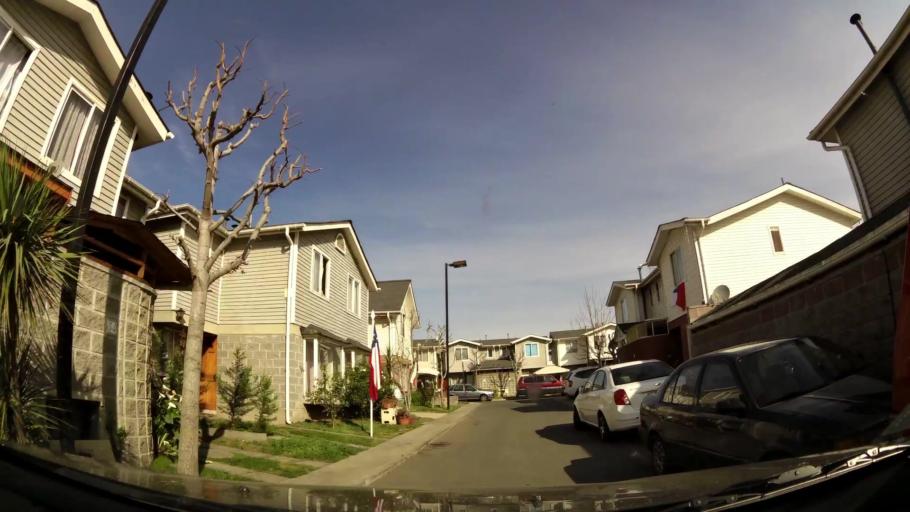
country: CL
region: Santiago Metropolitan
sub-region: Provincia de Cordillera
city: Puente Alto
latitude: -33.5896
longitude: -70.5586
